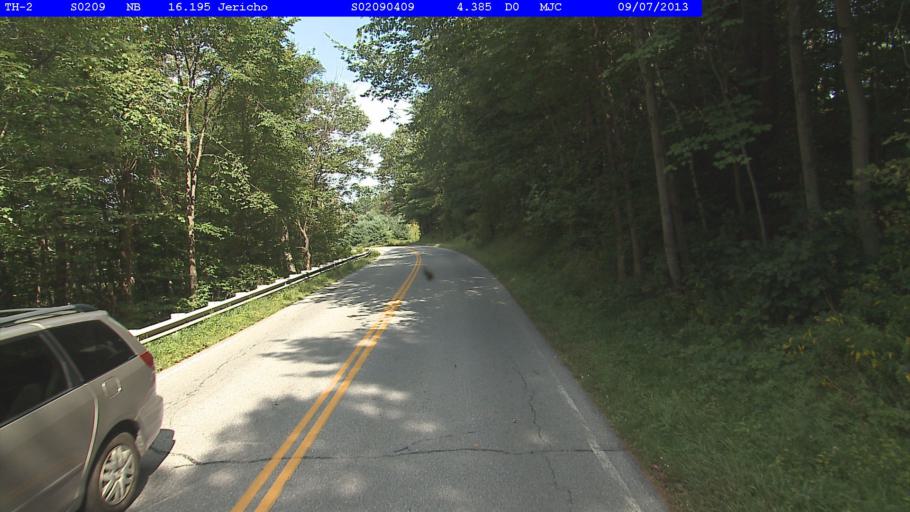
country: US
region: Vermont
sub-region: Chittenden County
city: Jericho
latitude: 44.4869
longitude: -72.9778
